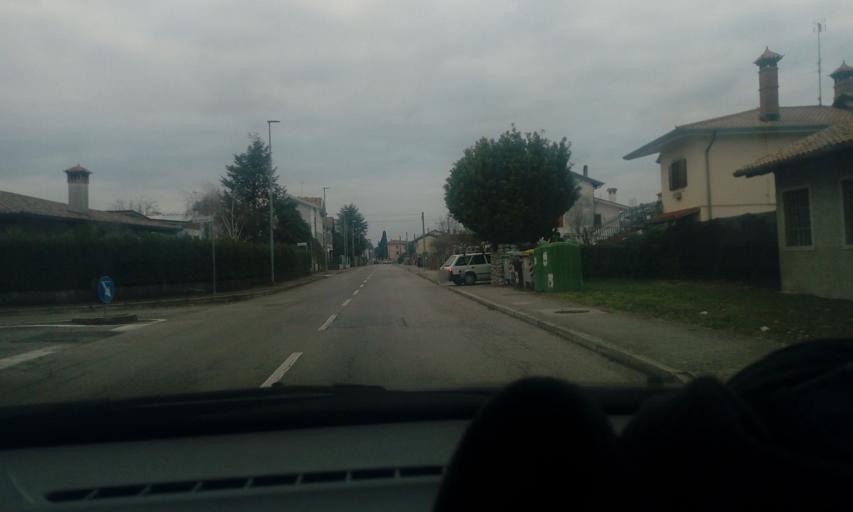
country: IT
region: Friuli Venezia Giulia
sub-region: Provincia di Udine
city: Campolongo al Torre-Cavenzano
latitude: 45.8512
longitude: 13.3831
